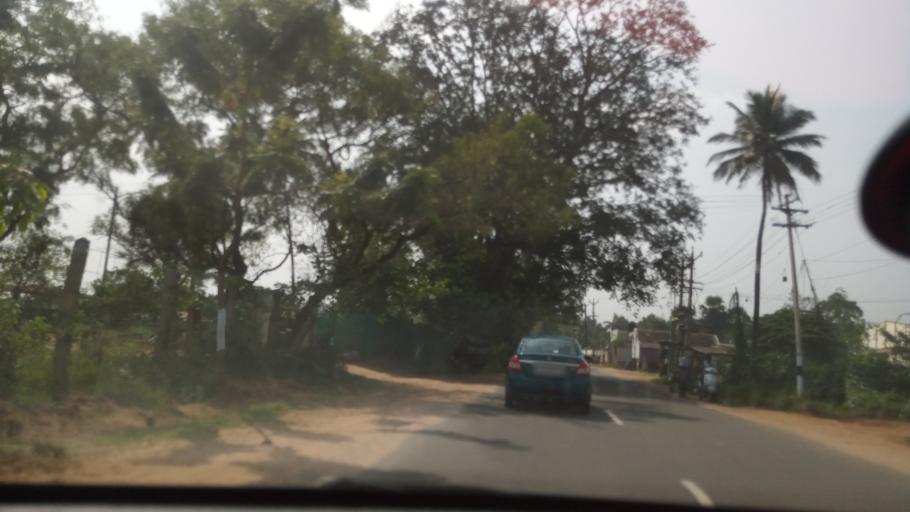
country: IN
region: Tamil Nadu
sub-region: Coimbatore
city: Perur
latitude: 10.9979
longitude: 76.8506
